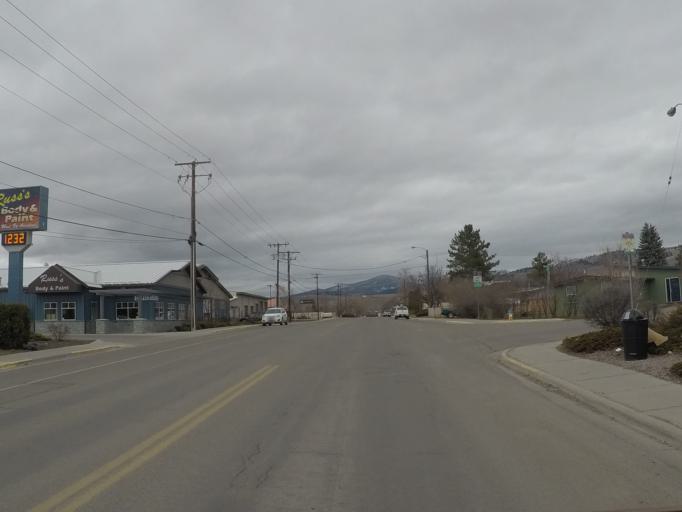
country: US
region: Montana
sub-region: Missoula County
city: Missoula
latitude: 46.8817
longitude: -114.0184
